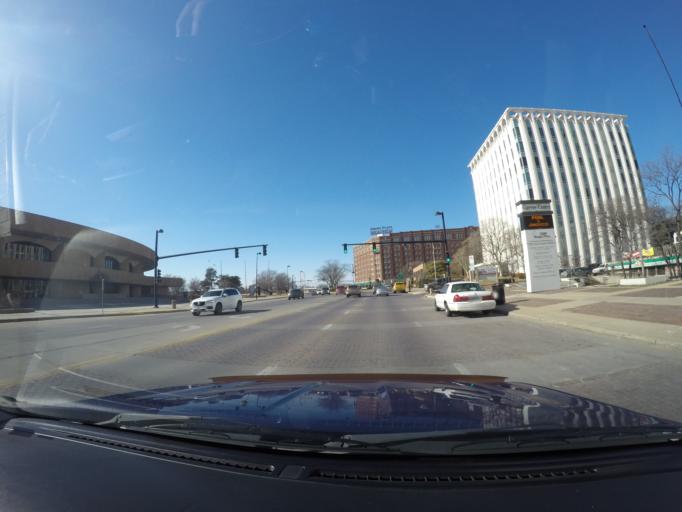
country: US
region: Kansas
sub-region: Sedgwick County
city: Wichita
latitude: 37.6860
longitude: -97.3402
